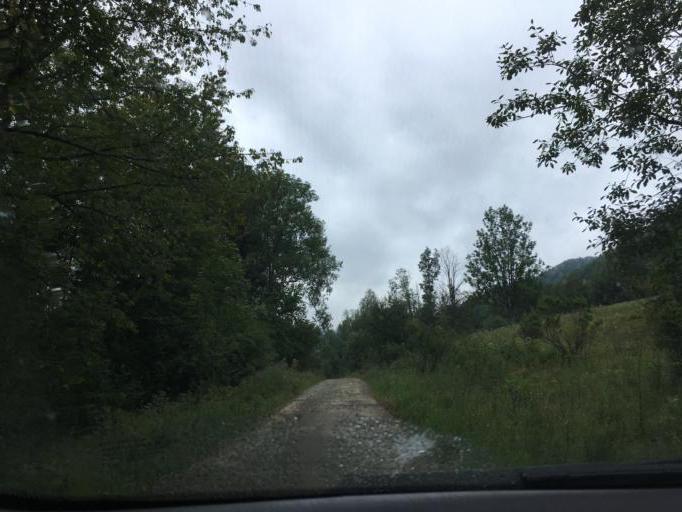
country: PL
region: Subcarpathian Voivodeship
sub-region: Powiat bieszczadzki
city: Lutowiska
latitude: 49.1604
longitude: 22.6279
